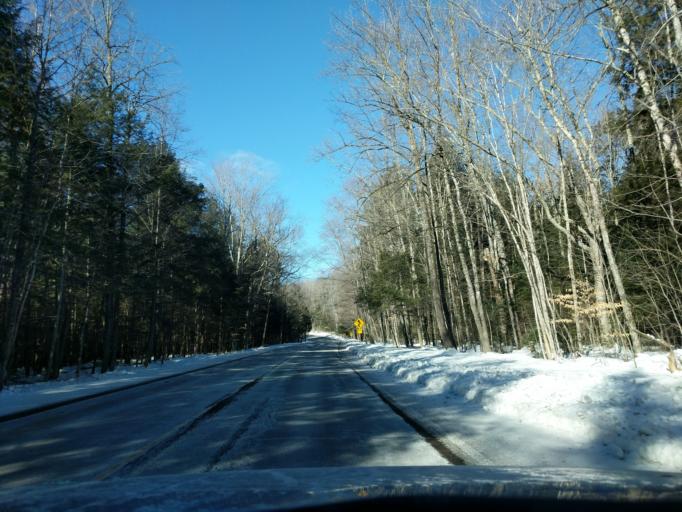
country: US
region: Wisconsin
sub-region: Menominee County
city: Keshena
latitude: 45.1105
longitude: -88.6407
